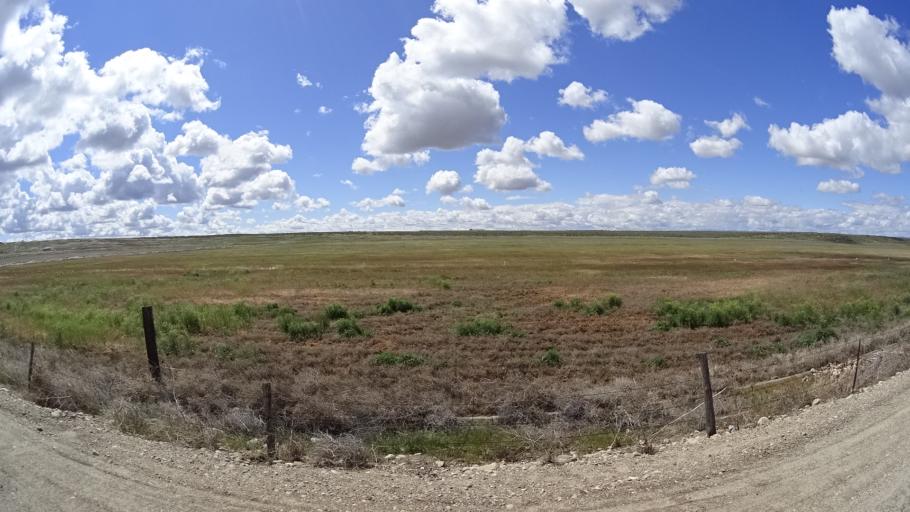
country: US
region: Idaho
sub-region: Ada County
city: Boise
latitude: 43.4853
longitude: -116.2440
